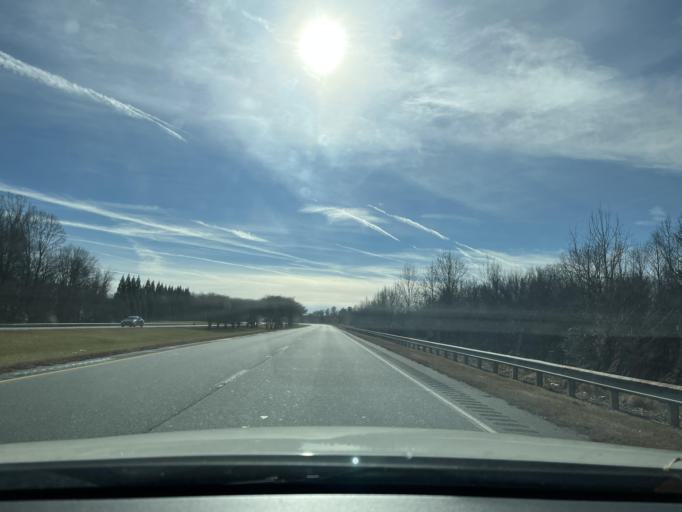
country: US
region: North Carolina
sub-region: Guilford County
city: Greensboro
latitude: 36.0337
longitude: -79.7723
